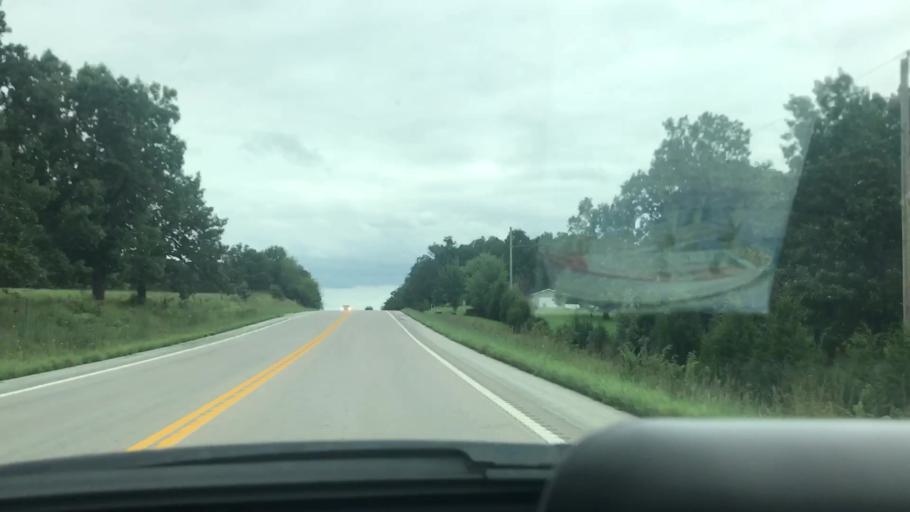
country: US
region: Missouri
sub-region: Dallas County
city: Buffalo
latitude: 37.7118
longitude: -93.1156
